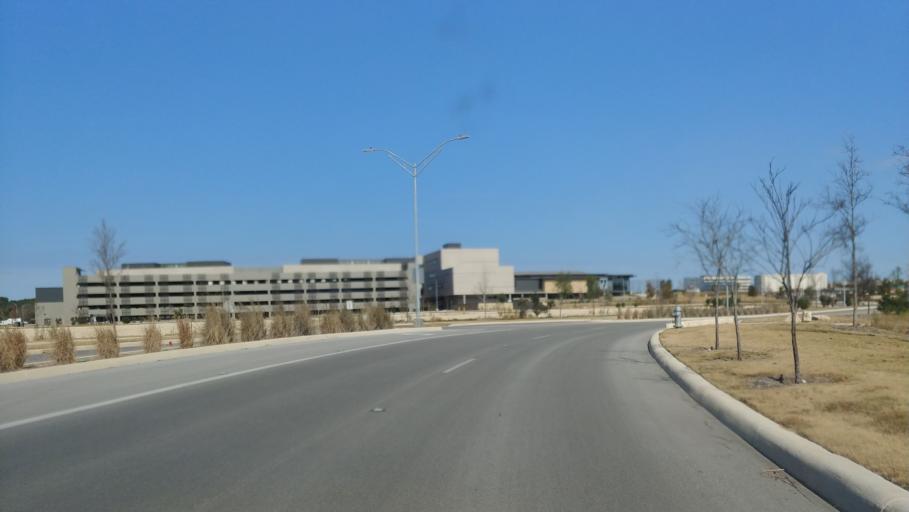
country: US
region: Texas
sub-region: Bexar County
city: Shavano Park
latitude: 29.5798
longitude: -98.6017
